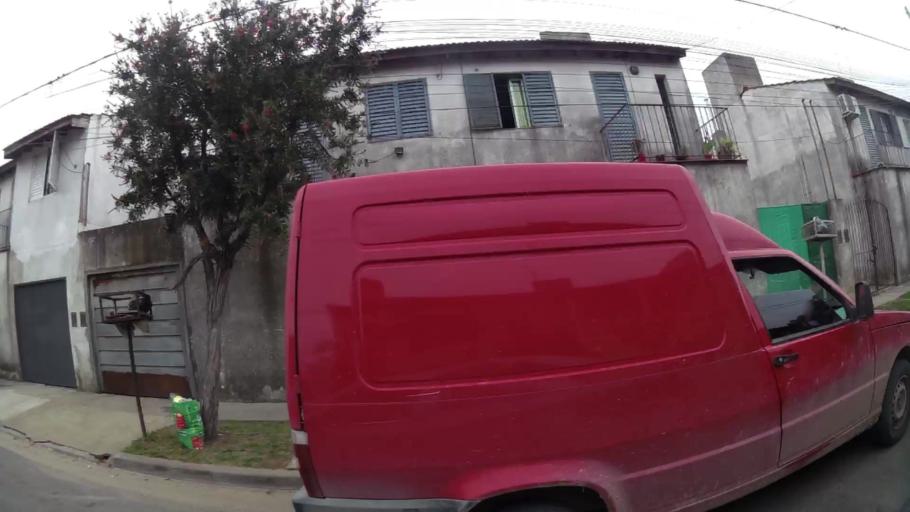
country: AR
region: Buenos Aires
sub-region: Partido de Campana
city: Campana
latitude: -34.1867
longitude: -58.9386
